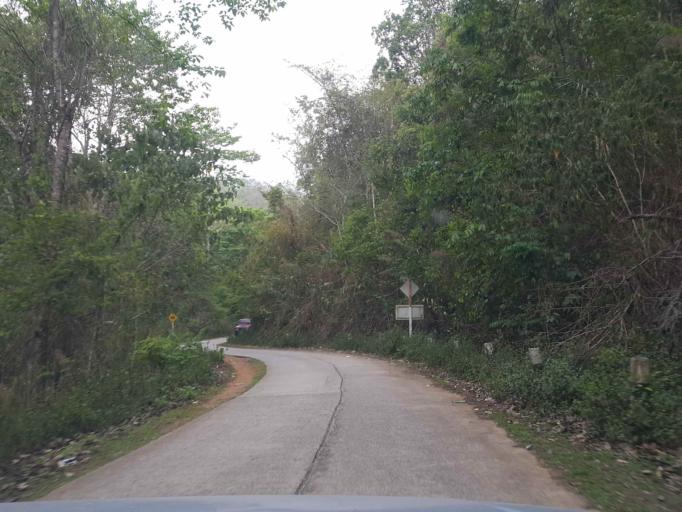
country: TH
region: Chiang Mai
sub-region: Amphoe Chiang Dao
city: Chiang Dao
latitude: 19.3779
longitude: 98.7628
